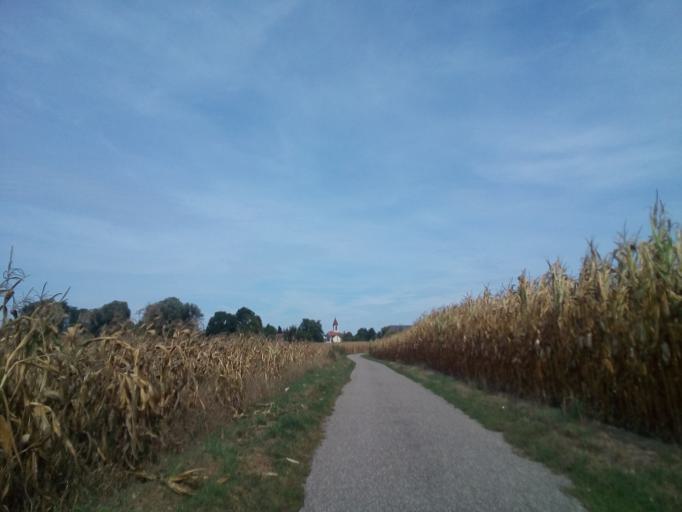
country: DE
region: Baden-Wuerttemberg
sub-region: Karlsruhe Region
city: Ottenhofen
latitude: 48.7330
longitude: 8.1227
